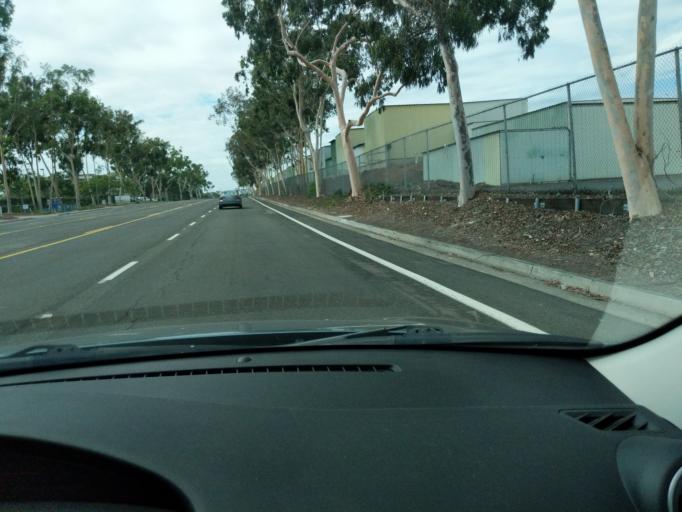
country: US
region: California
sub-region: San Diego County
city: San Diego
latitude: 32.8099
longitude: -117.1358
